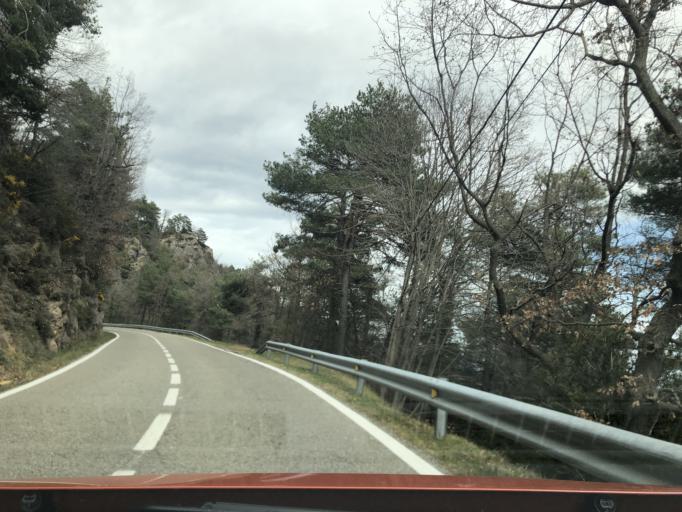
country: ES
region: Catalonia
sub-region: Provincia de Barcelona
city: Capolat
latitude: 42.0918
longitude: 1.7639
